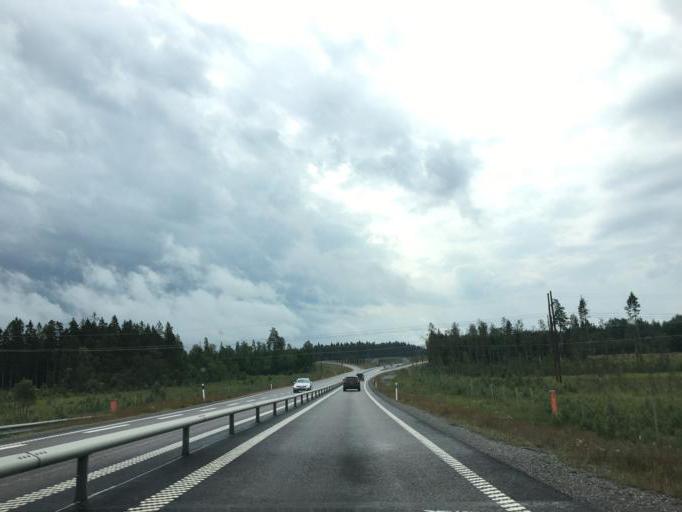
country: SE
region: Soedermanland
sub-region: Katrineholms Kommun
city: Katrineholm
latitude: 58.9975
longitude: 16.2546
